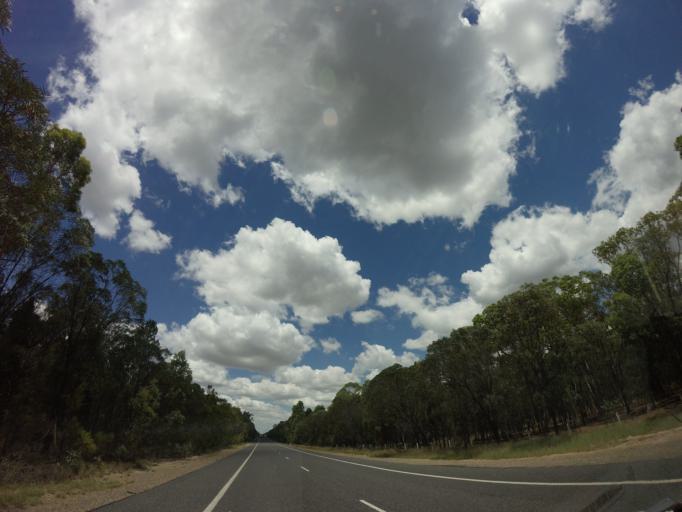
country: AU
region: Queensland
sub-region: Western Downs
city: Dalby
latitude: -27.9736
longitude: 151.0594
